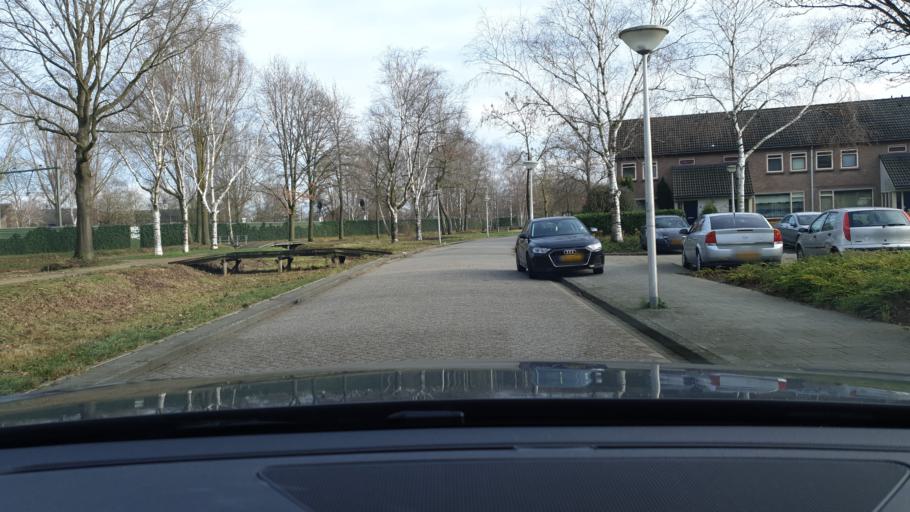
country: NL
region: North Brabant
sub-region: Gemeente Eindhoven
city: Muschberg en Geestenberg
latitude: 51.4422
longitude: 5.5169
